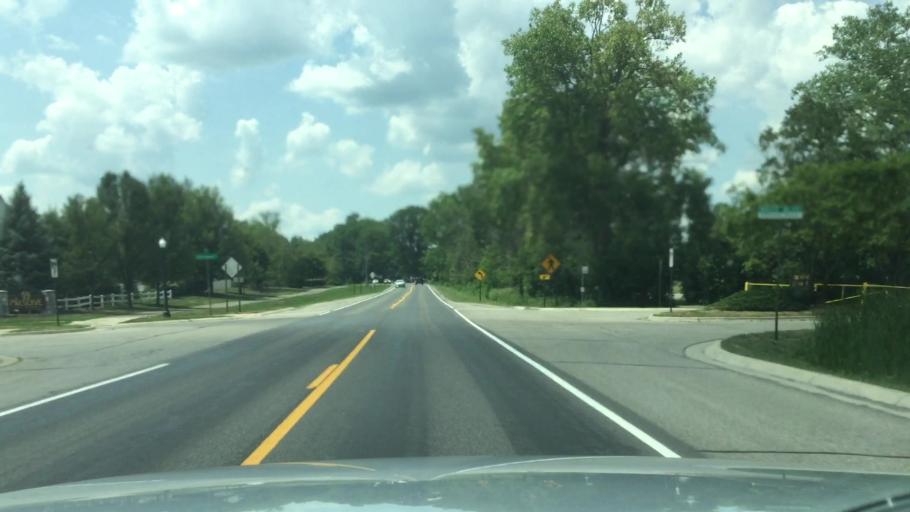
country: US
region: Michigan
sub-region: Washtenaw County
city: Ypsilanti
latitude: 42.2032
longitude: -83.5979
